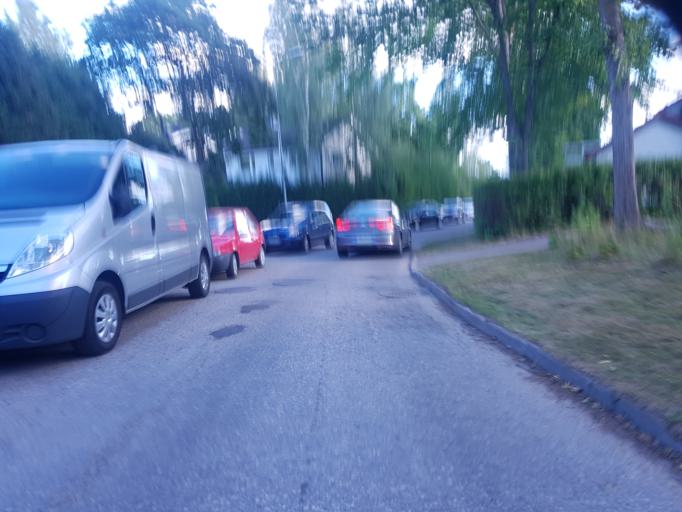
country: FI
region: Uusimaa
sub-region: Helsinki
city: Vantaa
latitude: 60.2715
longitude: 24.9838
